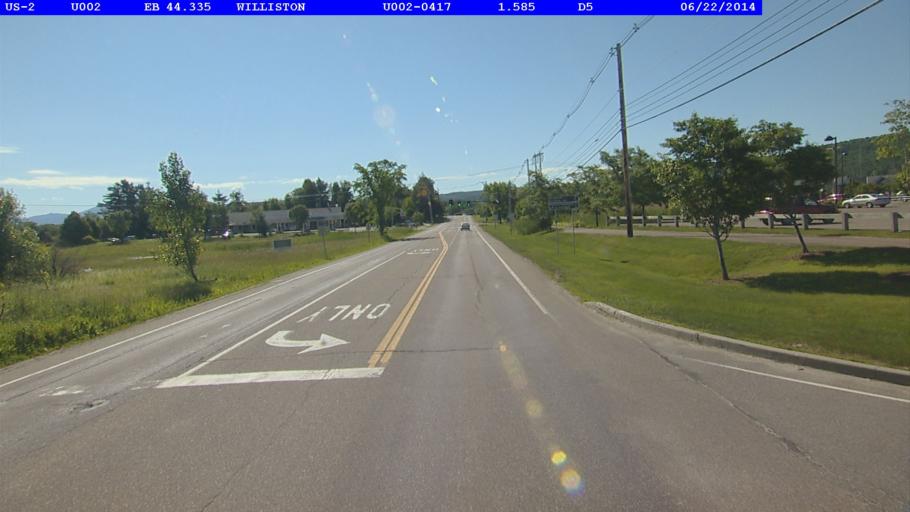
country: US
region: Vermont
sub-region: Chittenden County
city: Williston
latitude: 44.4483
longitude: -73.1081
